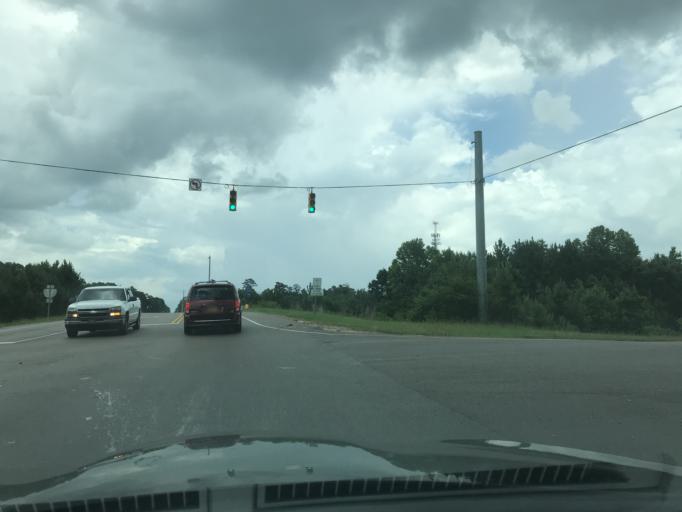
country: US
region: North Carolina
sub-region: Wake County
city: Knightdale
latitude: 35.8469
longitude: -78.5244
